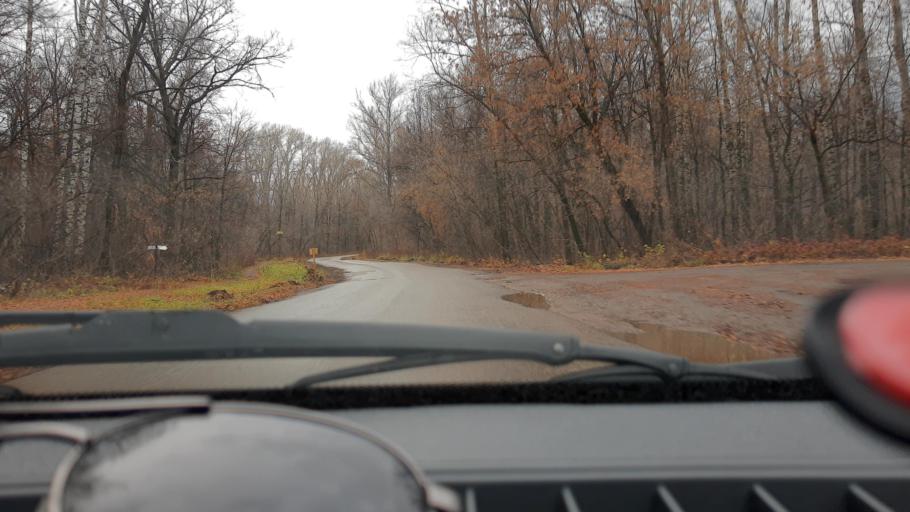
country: RU
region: Bashkortostan
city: Ufa
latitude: 54.7918
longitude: 56.1567
